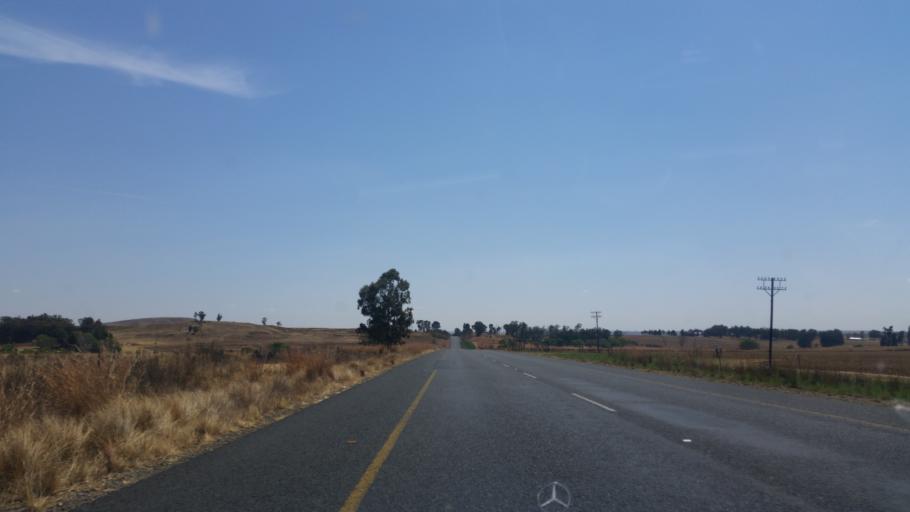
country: ZA
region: Orange Free State
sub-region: Thabo Mofutsanyana District Municipality
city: Phuthaditjhaba
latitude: -28.2368
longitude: 28.7073
